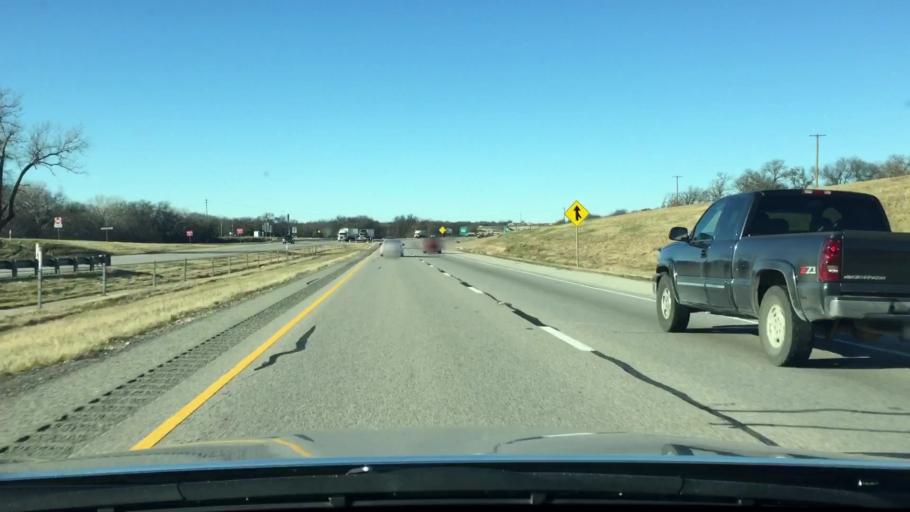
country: US
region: Texas
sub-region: Johnson County
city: Grandview
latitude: 32.2868
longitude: -97.1774
